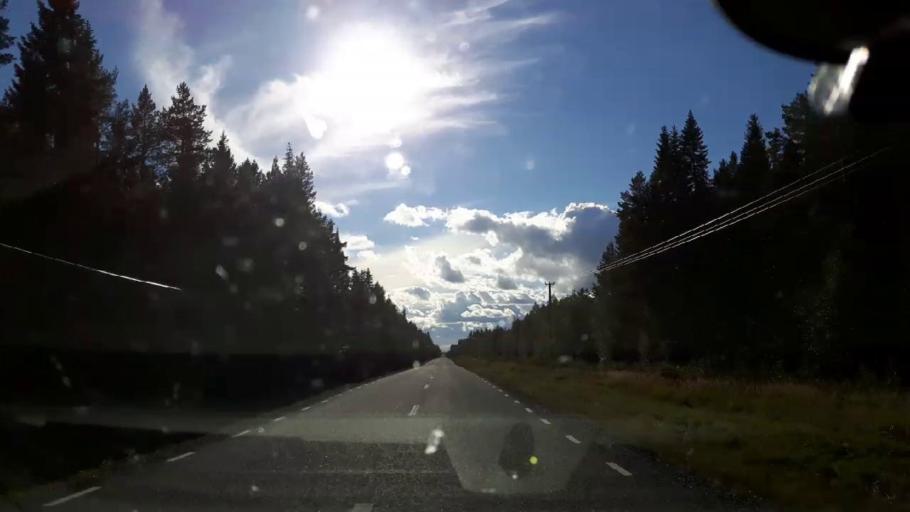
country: SE
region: Jaemtland
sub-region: Stroemsunds Kommun
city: Stroemsund
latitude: 63.5620
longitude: 15.5805
